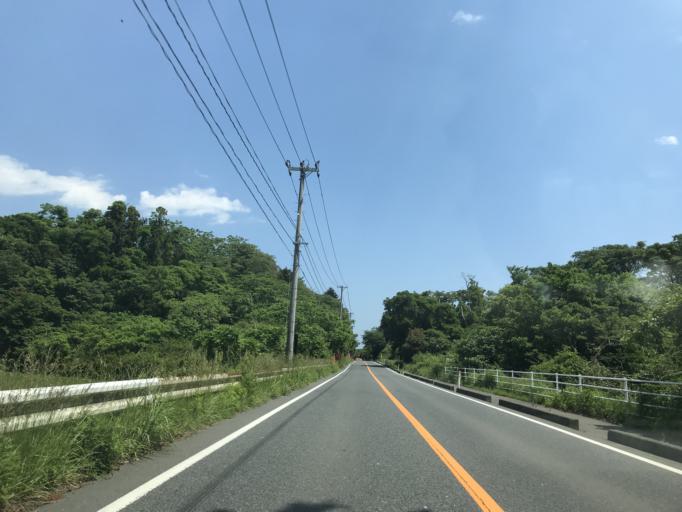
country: JP
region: Miyagi
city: Matsushima
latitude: 38.3812
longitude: 141.1215
